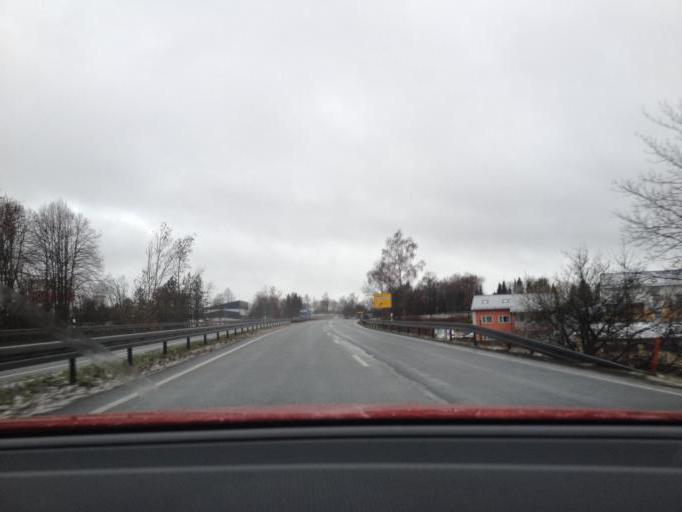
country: DE
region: Bavaria
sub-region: Upper Franconia
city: Hof
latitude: 50.2884
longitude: 11.9202
